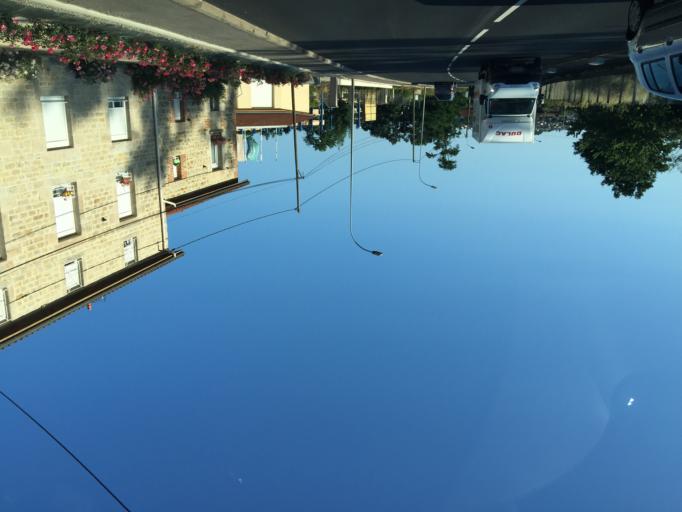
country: FR
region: Rhone-Alpes
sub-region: Departement de la Loire
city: La Talaudiere
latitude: 45.4758
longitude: 4.4430
